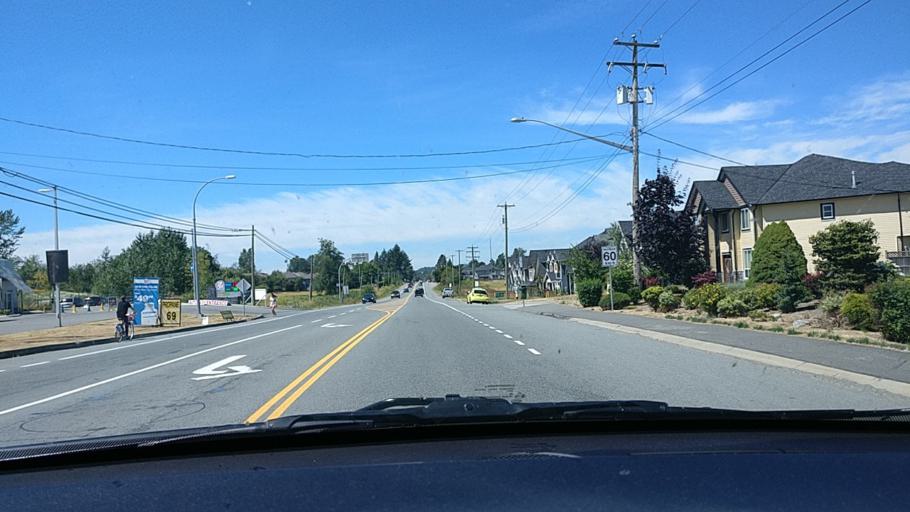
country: CA
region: British Columbia
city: Aldergrove
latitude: 49.0574
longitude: -122.4489
